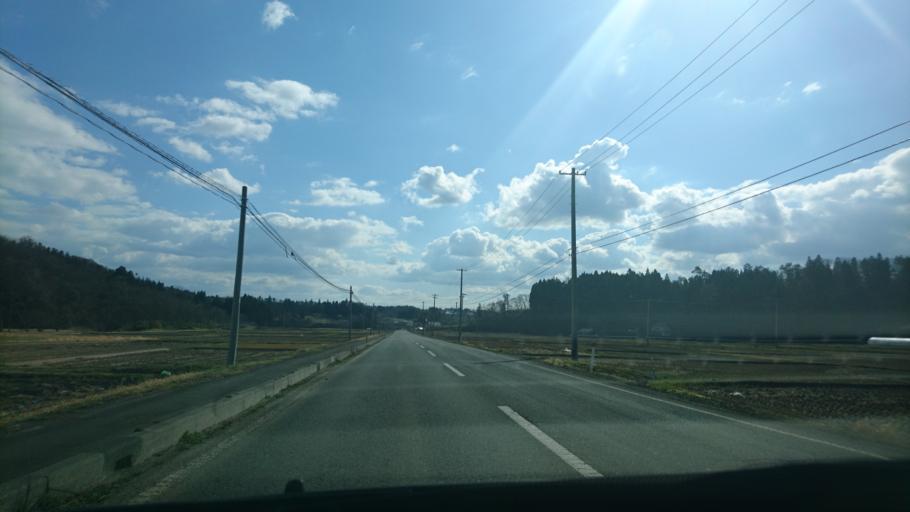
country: JP
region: Iwate
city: Kitakami
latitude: 39.2395
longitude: 141.1985
